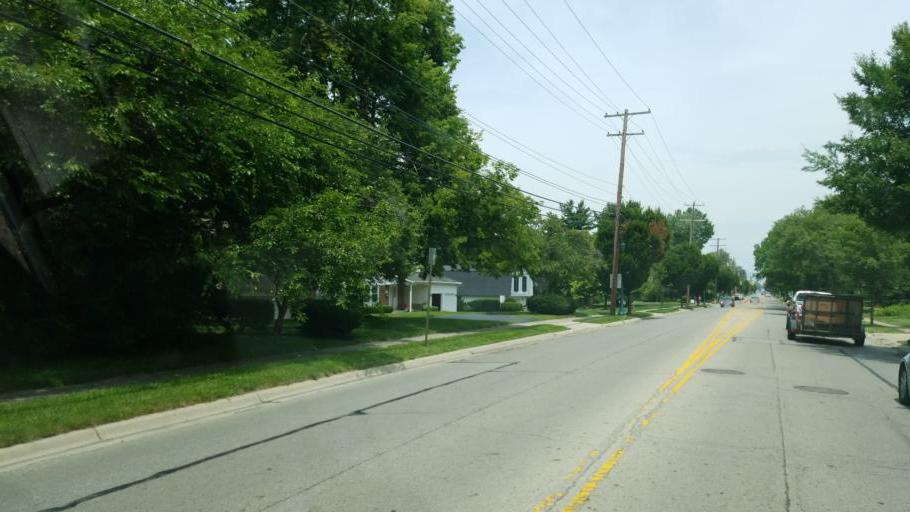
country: US
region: Ohio
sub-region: Franklin County
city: Upper Arlington
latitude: 40.0446
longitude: -83.0667
